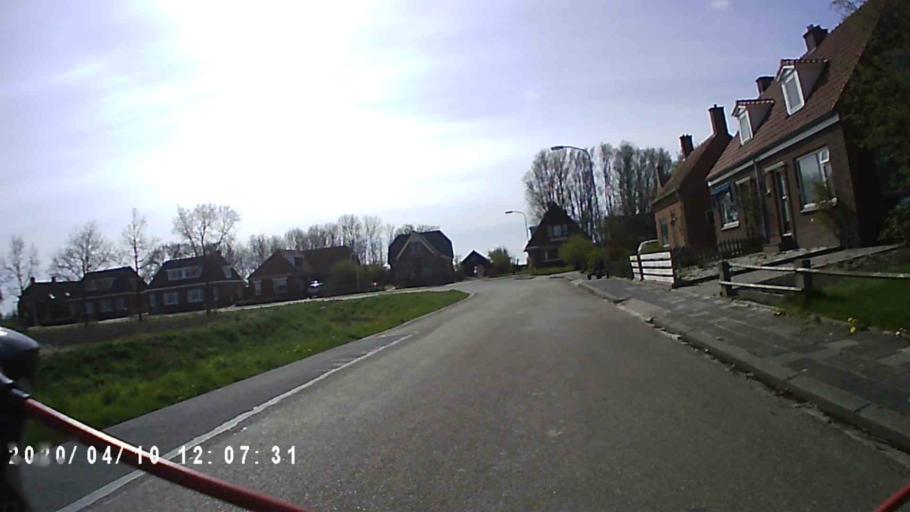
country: NL
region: Groningen
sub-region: Gemeente De Marne
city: Ulrum
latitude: 53.3882
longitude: 6.3655
